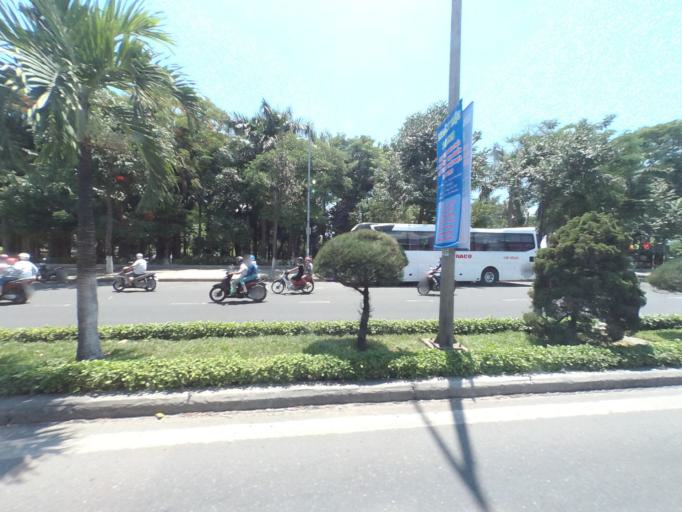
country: VN
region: Da Nang
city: Thanh Khe
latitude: 16.0630
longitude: 108.2038
